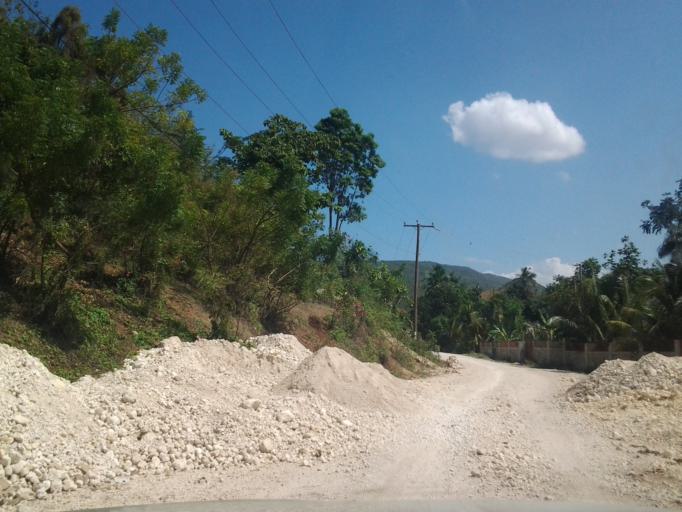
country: HT
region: Ouest
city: Tigwav
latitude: 18.4402
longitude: -72.8415
